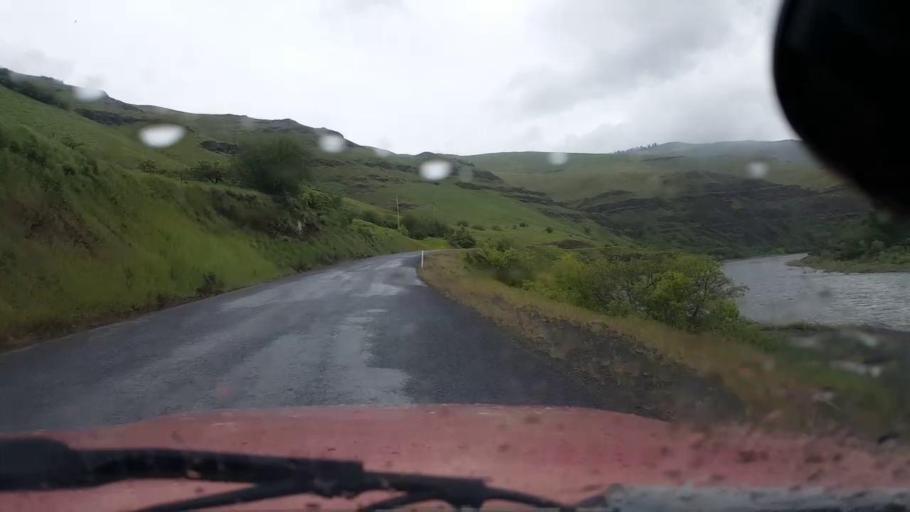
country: US
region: Washington
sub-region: Asotin County
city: Asotin
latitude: 46.0402
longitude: -117.2654
